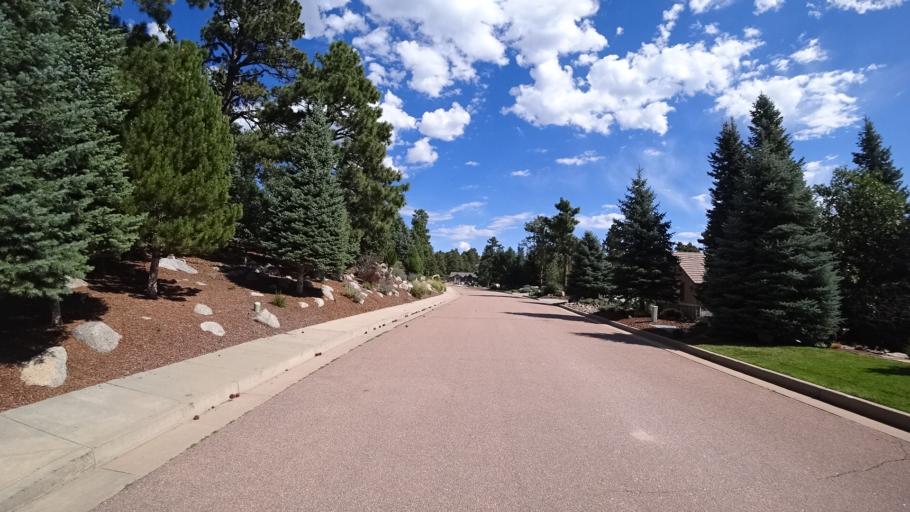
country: US
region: Colorado
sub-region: El Paso County
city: Fort Carson
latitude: 38.7448
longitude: -104.8399
